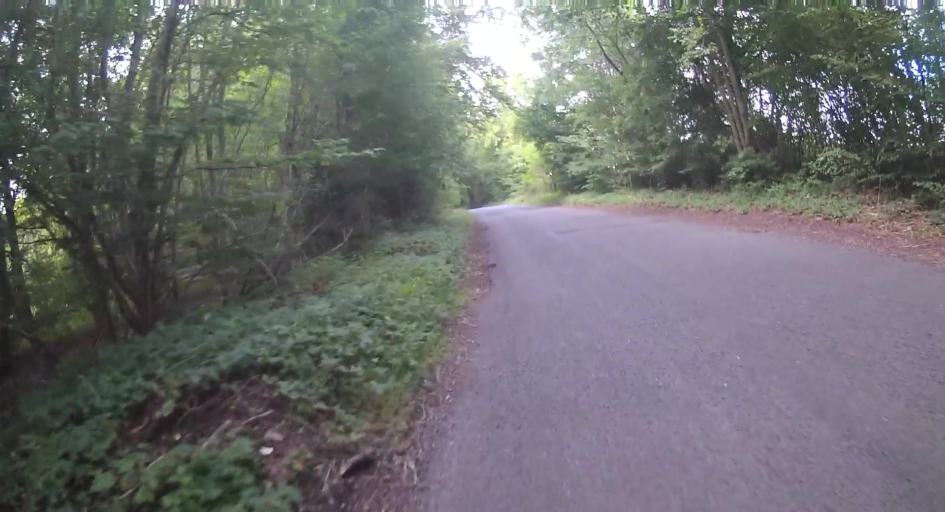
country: GB
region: England
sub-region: Hampshire
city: Overton
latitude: 51.1920
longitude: -1.2790
